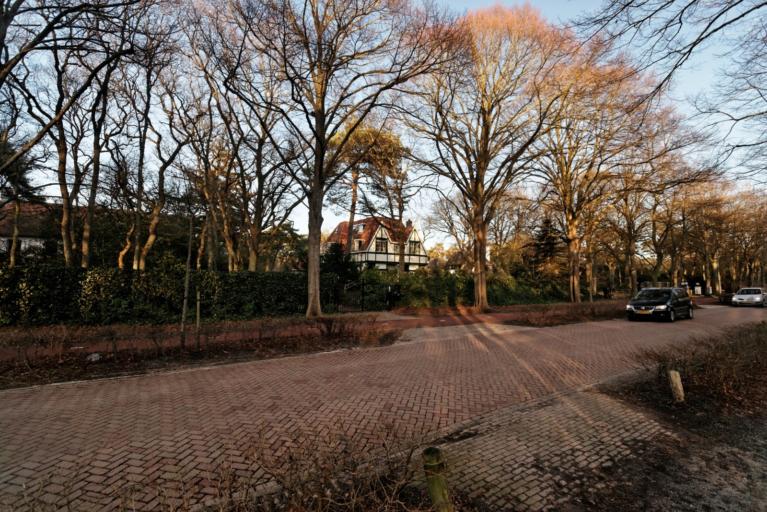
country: NL
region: North Holland
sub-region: Gemeente Heiloo
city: Heiloo
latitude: 52.6670
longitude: 4.6841
